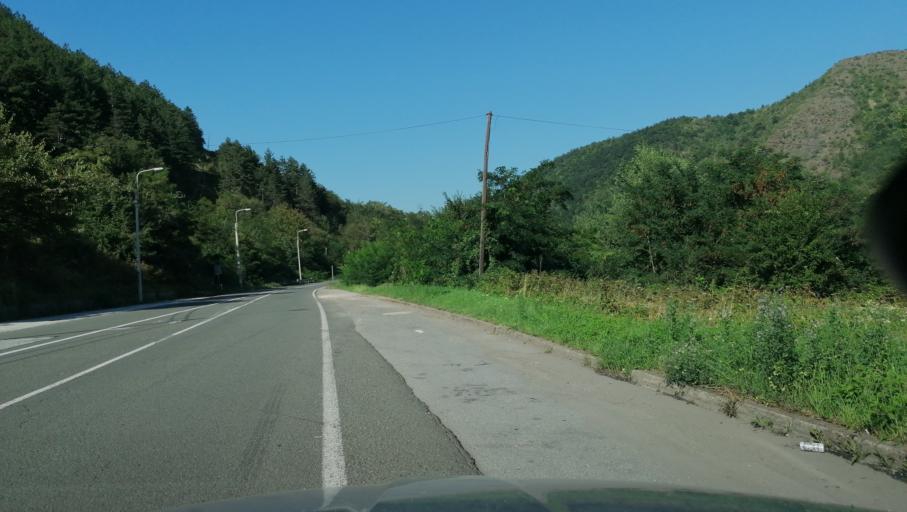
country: RS
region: Central Serbia
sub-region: Raski Okrug
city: Kraljevo
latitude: 43.6537
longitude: 20.5574
